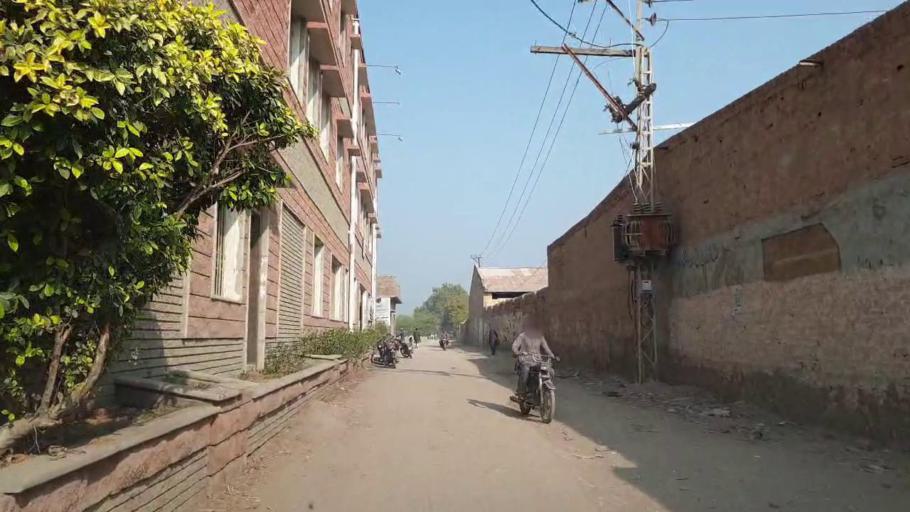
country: PK
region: Sindh
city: Mirpur Khas
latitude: 25.5377
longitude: 69.0247
